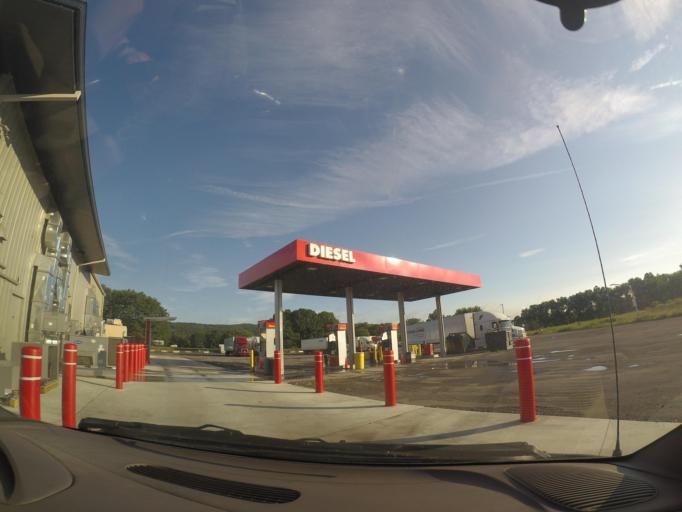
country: US
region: New York
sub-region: Tioga County
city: Owego
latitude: 42.0636
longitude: -76.3235
